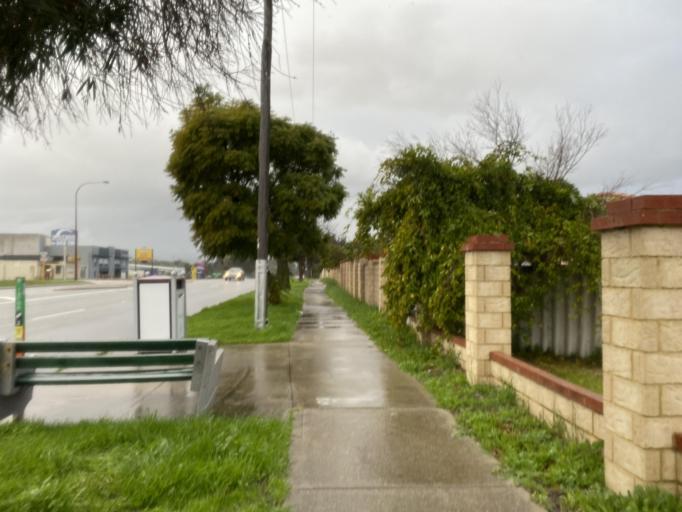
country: AU
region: Western Australia
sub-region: Canning
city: Queens Park
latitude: -31.9977
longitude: 115.9512
